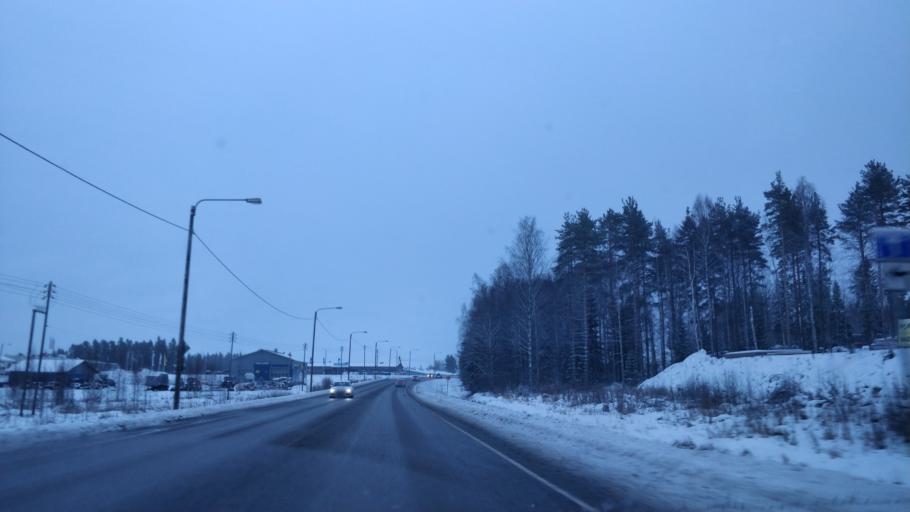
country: FI
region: Central Finland
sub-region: Saarijaervi-Viitasaari
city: Viitasaari
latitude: 63.0909
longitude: 25.8578
